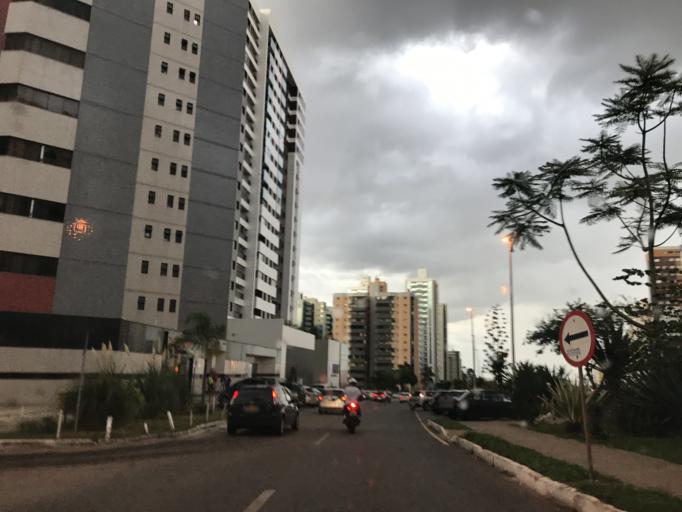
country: BR
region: Federal District
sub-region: Brasilia
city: Brasilia
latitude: -15.8355
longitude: -48.0147
